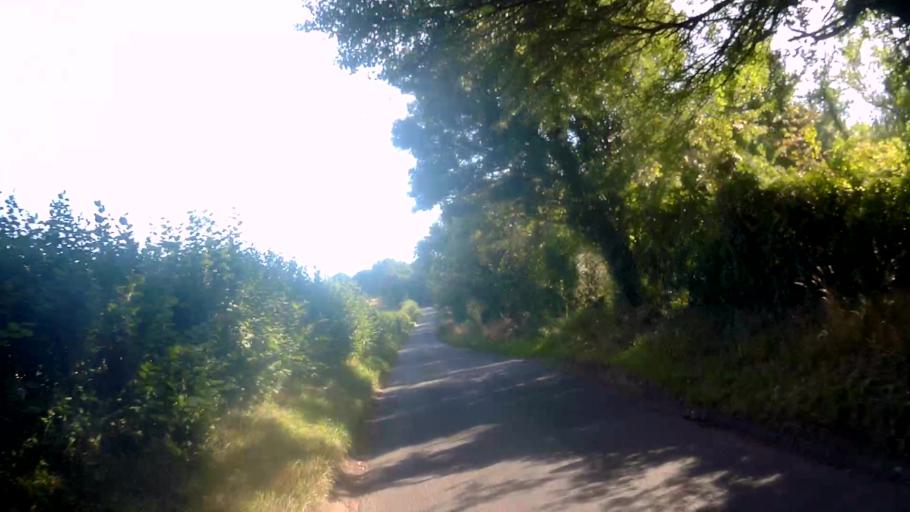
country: GB
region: England
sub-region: Hampshire
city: Kings Worthy
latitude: 51.1511
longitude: -1.2220
